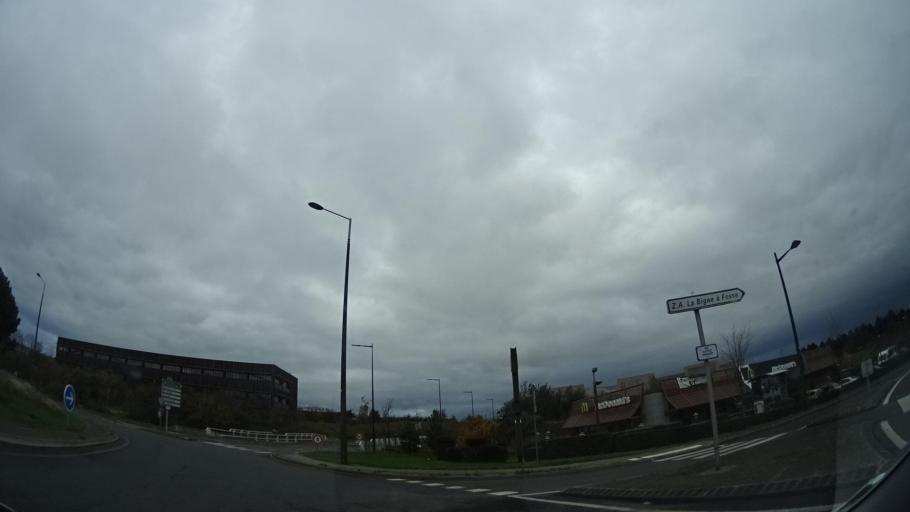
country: FR
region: Haute-Normandie
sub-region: Departement de la Seine-Maritime
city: Sainte-Adresse
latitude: 49.5253
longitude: 0.1064
